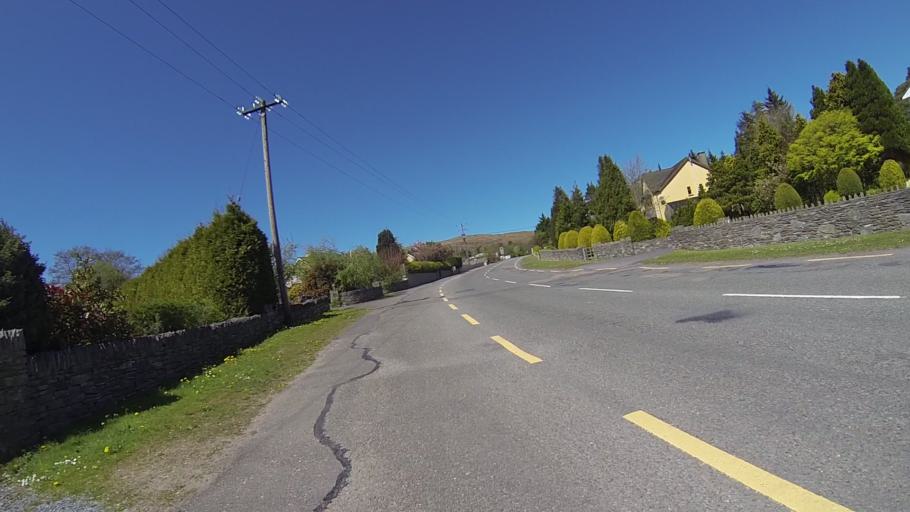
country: IE
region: Munster
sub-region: Ciarrai
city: Kenmare
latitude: 51.8856
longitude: -9.5946
